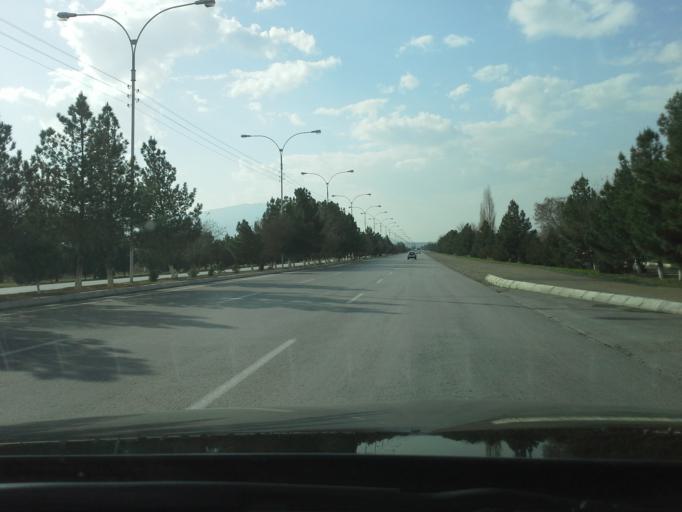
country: TM
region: Ahal
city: Abadan
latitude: 37.9735
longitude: 58.2558
